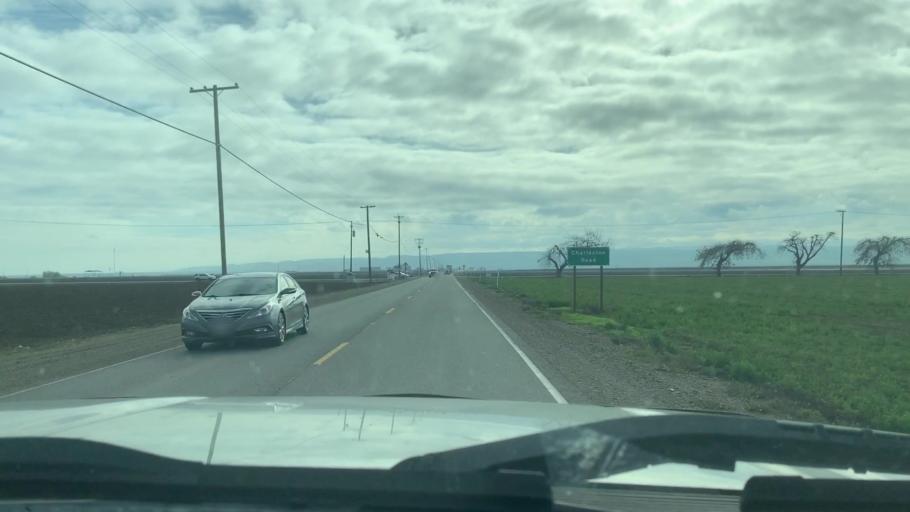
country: US
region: California
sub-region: Merced County
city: Los Banos
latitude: 36.9855
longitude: -120.8373
